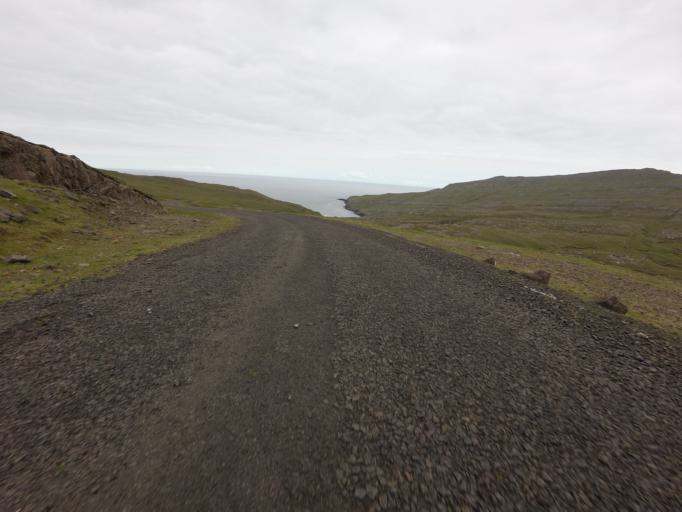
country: FO
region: Suduroy
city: Vagur
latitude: 61.4384
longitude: -6.7517
